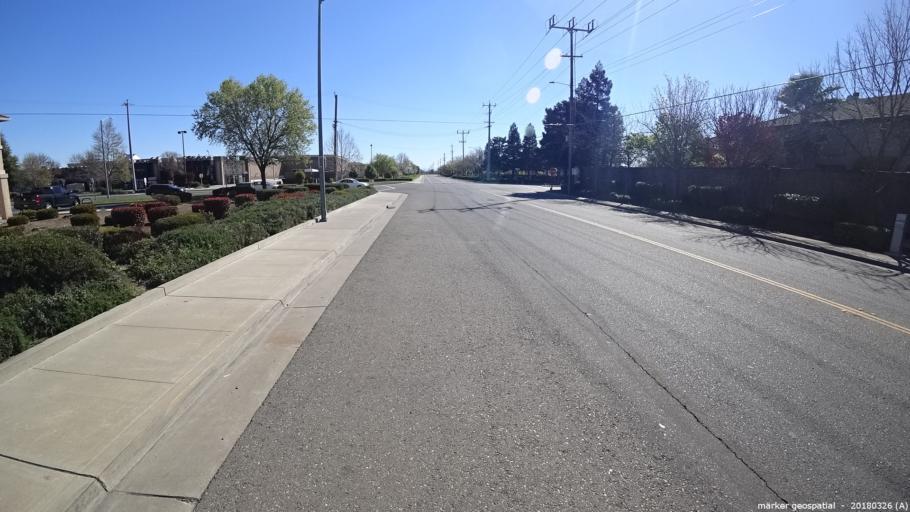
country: US
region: California
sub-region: Sacramento County
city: Laguna
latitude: 38.4526
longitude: -121.4058
